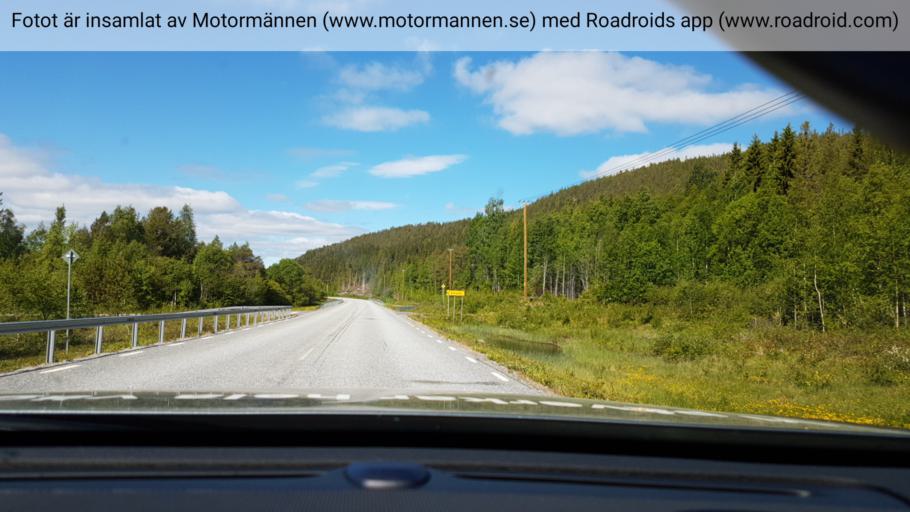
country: SE
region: Vaesterbotten
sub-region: Asele Kommun
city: Asele
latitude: 64.3221
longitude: 17.1006
